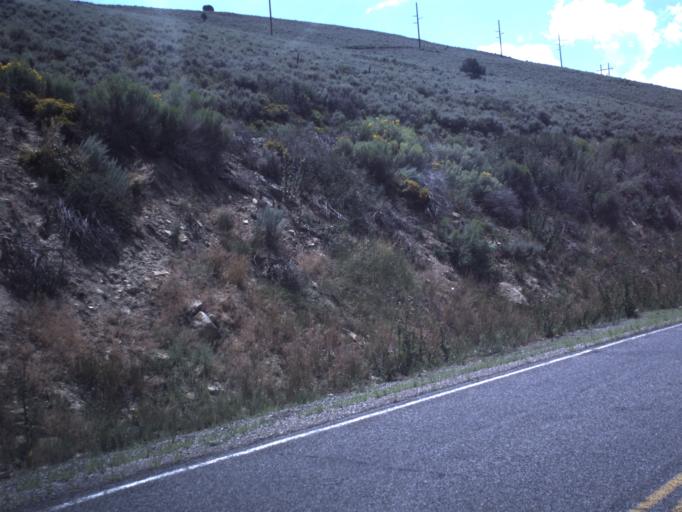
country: US
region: Utah
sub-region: Carbon County
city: Helper
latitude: 39.7801
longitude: -111.1348
